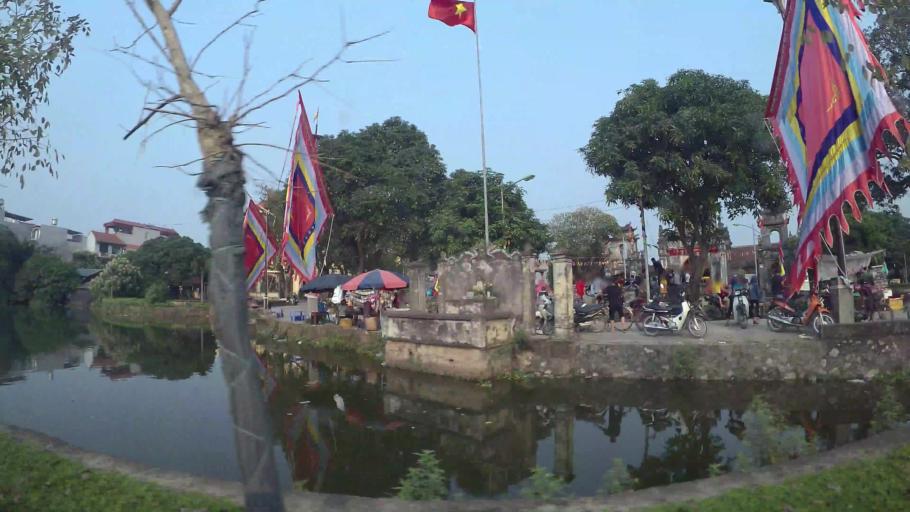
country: VN
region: Ha Noi
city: Thuong Tin
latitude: 20.8691
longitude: 105.8760
